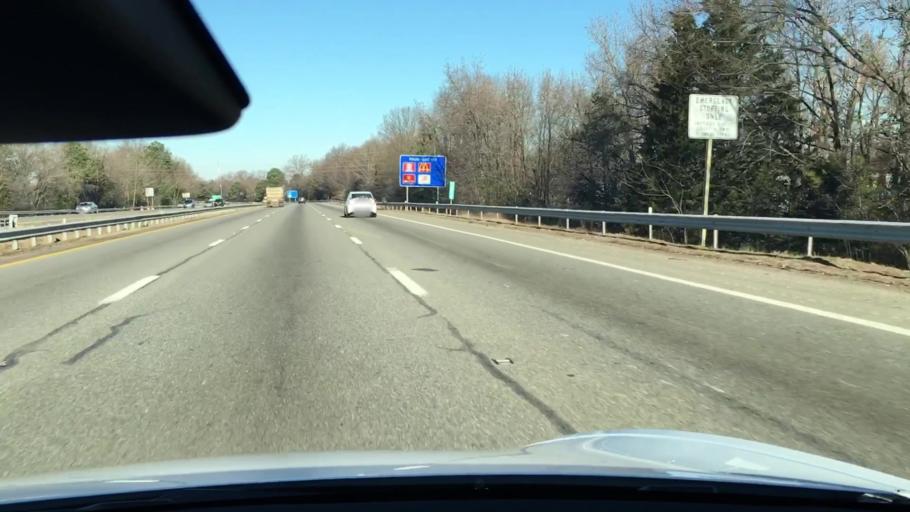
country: US
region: Virginia
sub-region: Henrico County
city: East Highland Park
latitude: 37.5499
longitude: -77.3986
